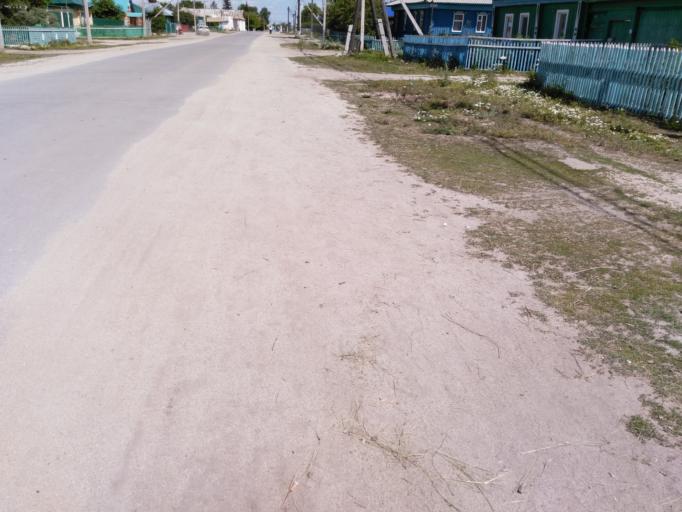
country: RU
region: Bashkortostan
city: Akhunovo
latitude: 54.2064
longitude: 59.5961
